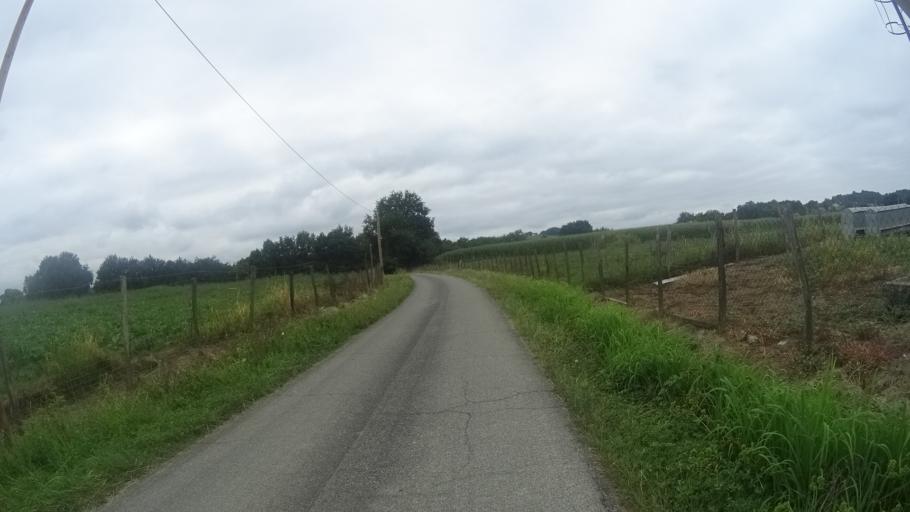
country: FR
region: Aquitaine
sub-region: Departement des Pyrenees-Atlantiques
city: Orthez
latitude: 43.4764
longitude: -0.7047
